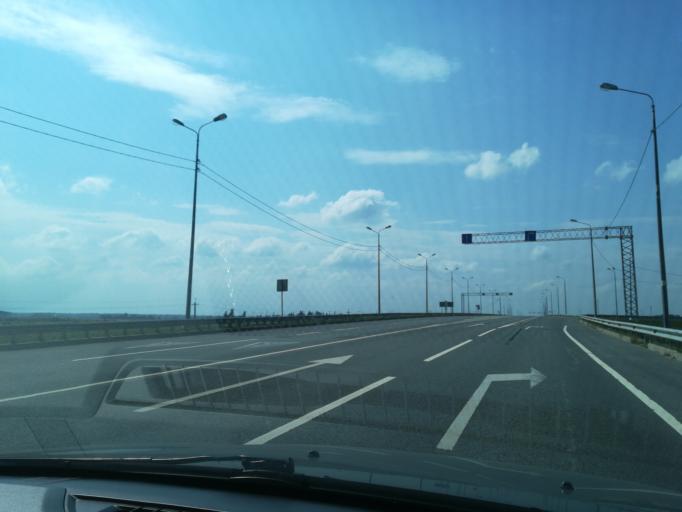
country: RU
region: Leningrad
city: Kingisepp
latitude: 59.5714
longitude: 28.7699
